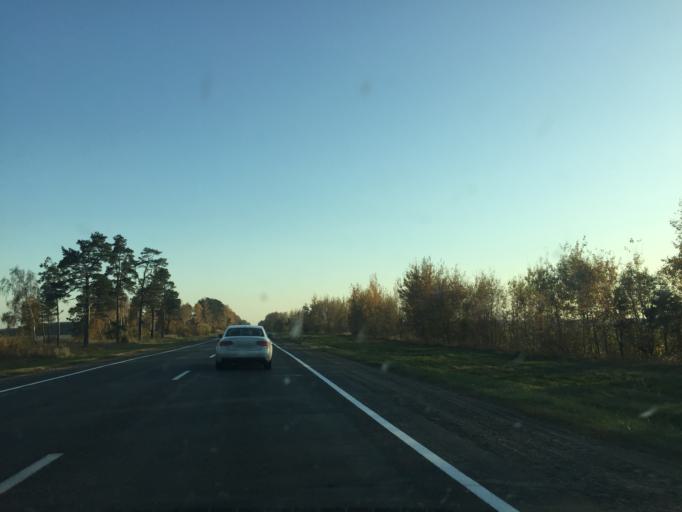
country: BY
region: Mogilev
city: Poselok Voskhod
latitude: 53.7424
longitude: 30.3660
